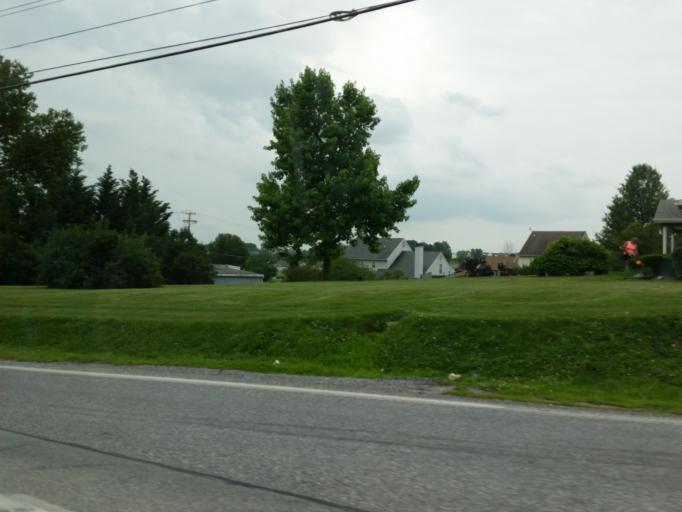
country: US
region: Pennsylvania
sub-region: York County
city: Emigsville
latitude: 40.0039
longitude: -76.7499
